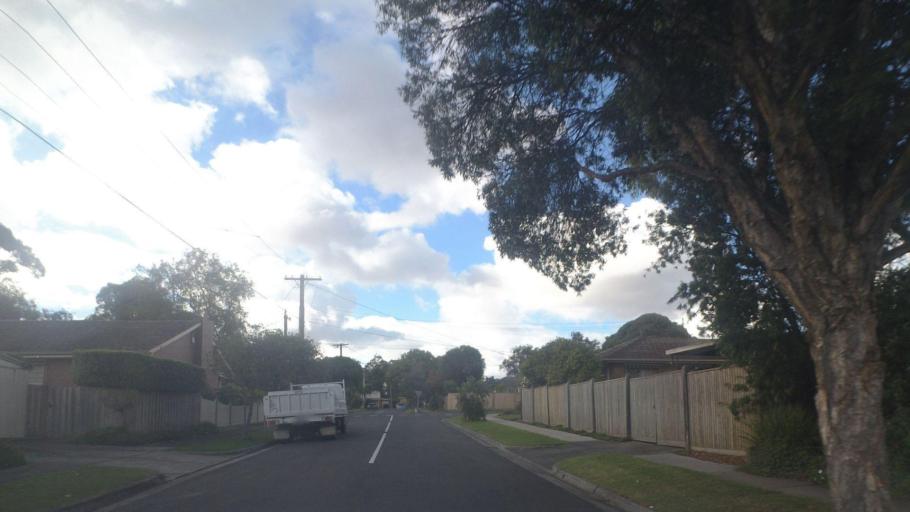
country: AU
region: Victoria
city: Forest Hill
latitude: -37.8396
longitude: 145.1863
